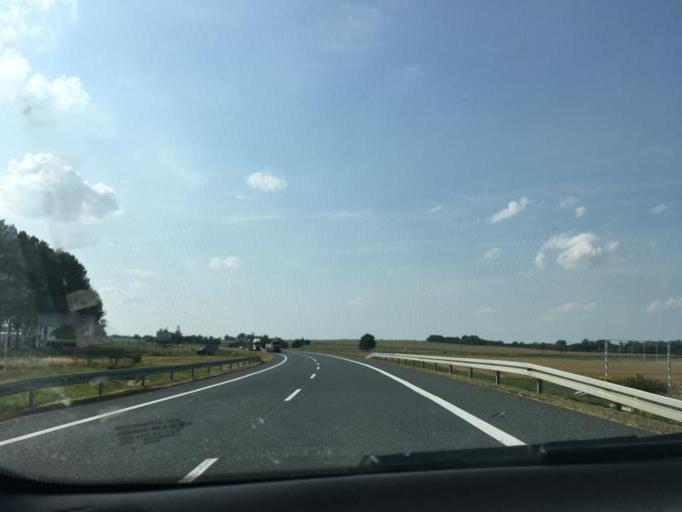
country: PL
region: Opole Voivodeship
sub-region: Powiat prudnicki
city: Prudnik
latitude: 50.3338
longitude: 17.5933
